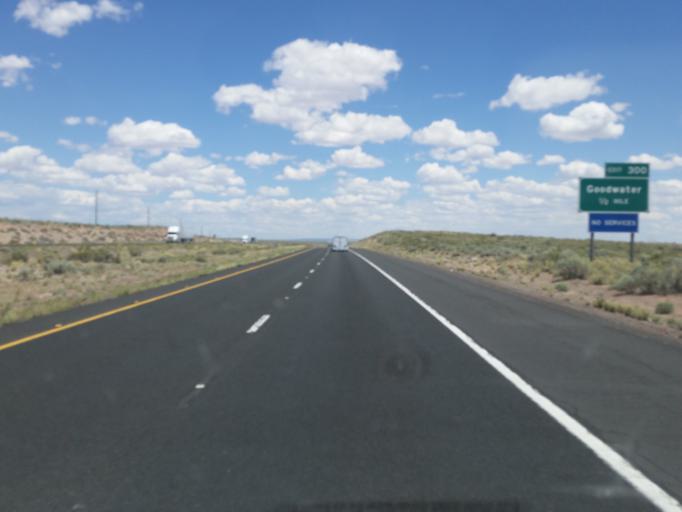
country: US
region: Arizona
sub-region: Navajo County
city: Holbrook
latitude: 34.9906
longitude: -109.9757
